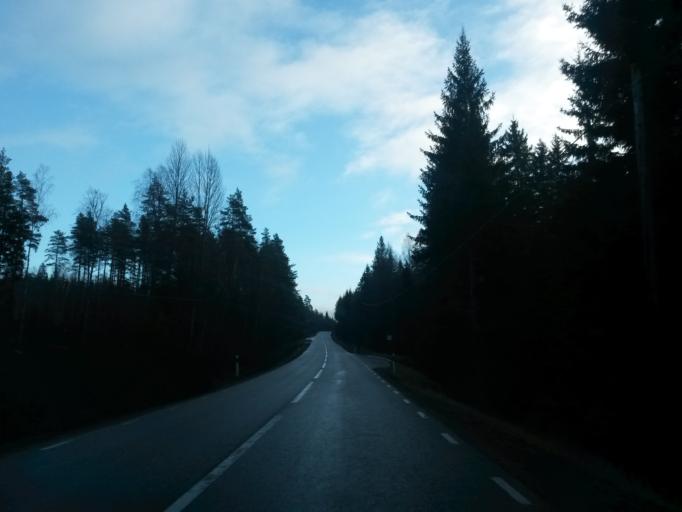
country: SE
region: Vaestra Goetaland
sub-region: Boras Kommun
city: Boras
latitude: 57.8483
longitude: 12.9520
